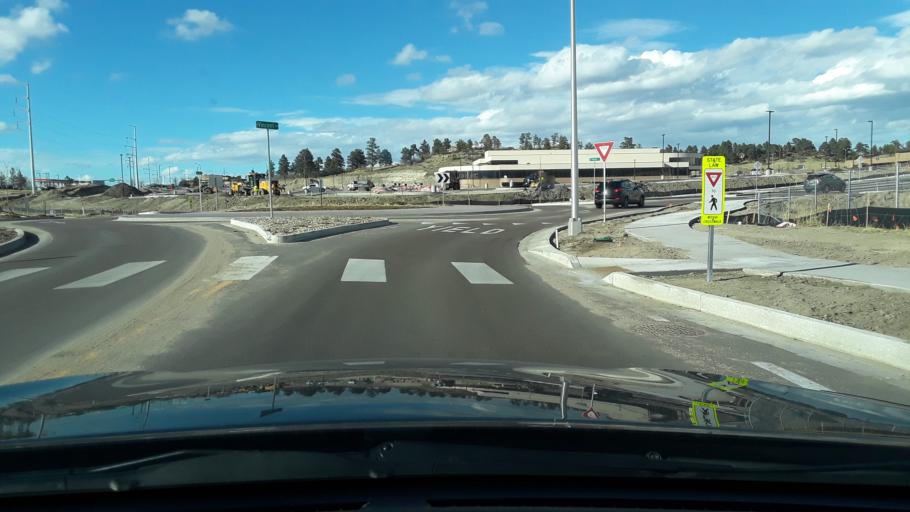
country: US
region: Colorado
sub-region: El Paso County
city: Air Force Academy
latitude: 38.9286
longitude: -104.8097
